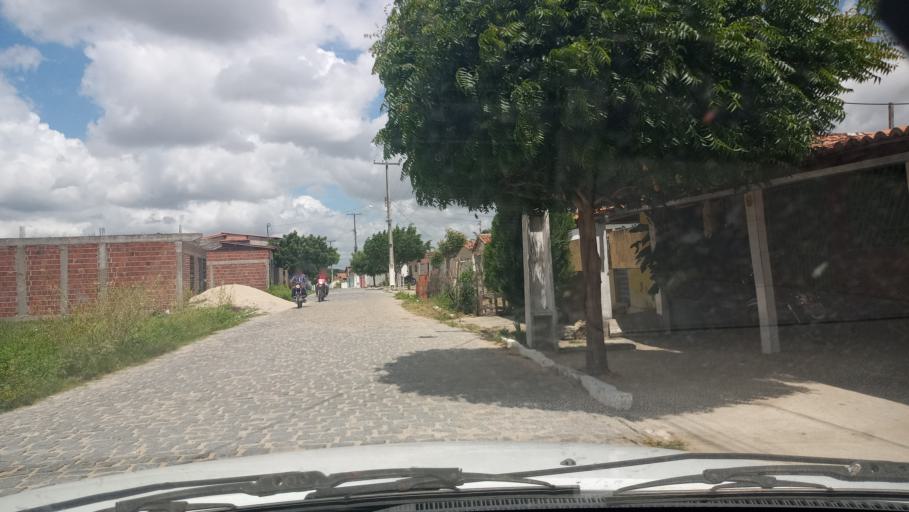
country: BR
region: Rio Grande do Norte
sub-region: Nova Cruz
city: Nova Cruz
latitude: -6.4573
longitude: -35.5785
